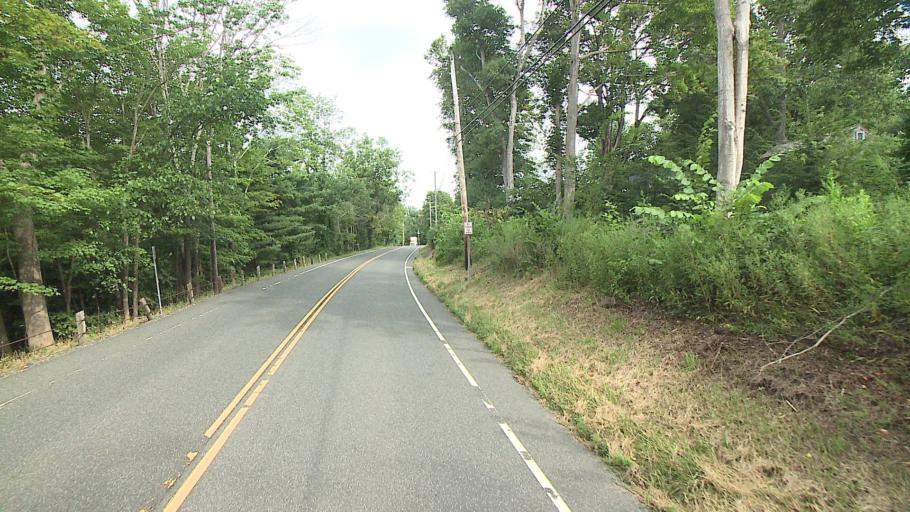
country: US
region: Connecticut
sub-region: Litchfield County
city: Woodbury
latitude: 41.5871
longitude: -73.2531
